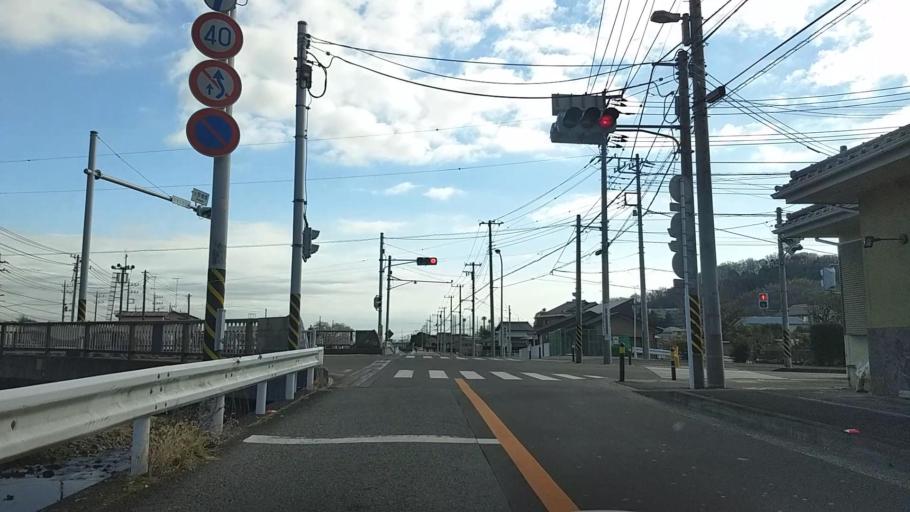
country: JP
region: Kanagawa
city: Atsugi
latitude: 35.4343
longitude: 139.3158
